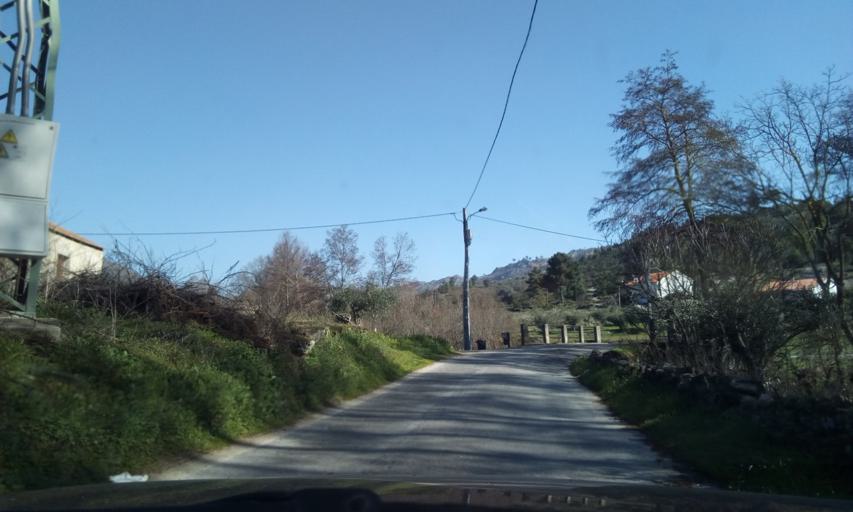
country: PT
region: Guarda
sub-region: Celorico da Beira
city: Celorico da Beira
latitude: 40.6877
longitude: -7.4017
